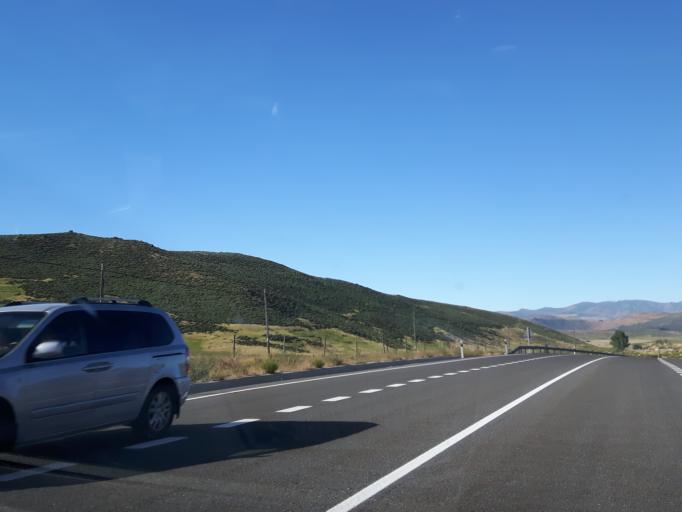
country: ES
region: Castille and Leon
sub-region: Provincia de Avila
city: Mengamunoz
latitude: 40.4756
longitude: -5.0130
